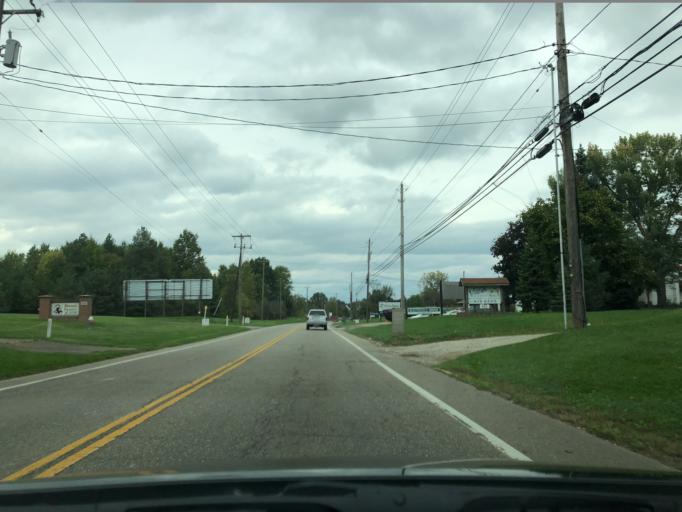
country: US
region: Ohio
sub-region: Summit County
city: Silver Lake
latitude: 41.1914
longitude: -81.5057
